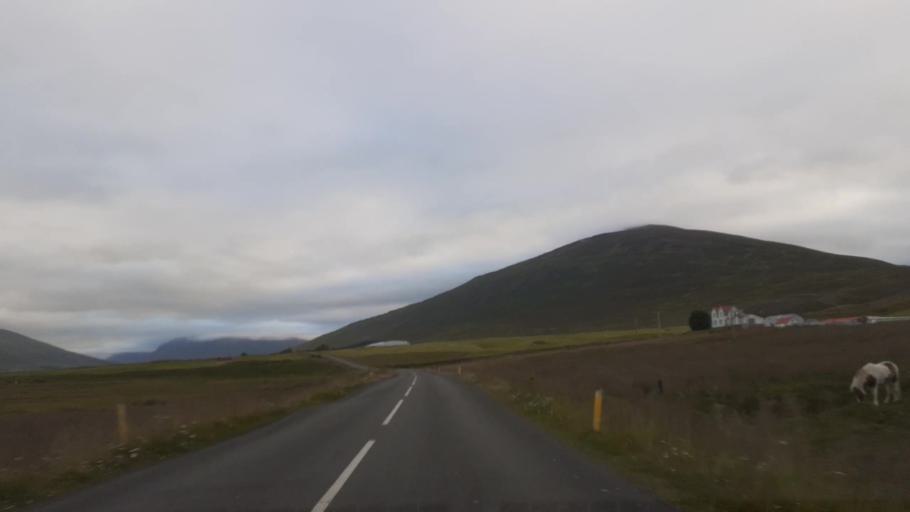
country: IS
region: Northeast
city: Dalvik
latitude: 65.9598
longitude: -18.5449
